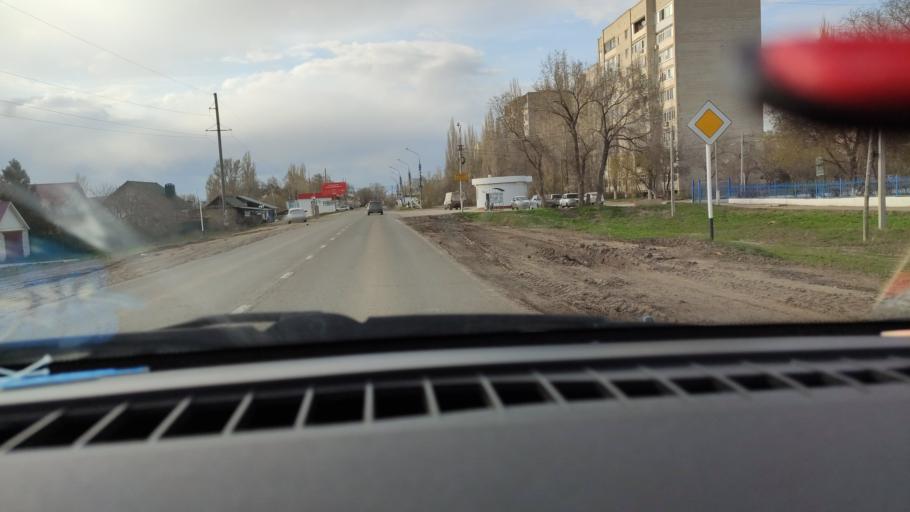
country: RU
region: Saratov
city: Privolzhskiy
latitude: 51.3906
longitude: 46.0356
